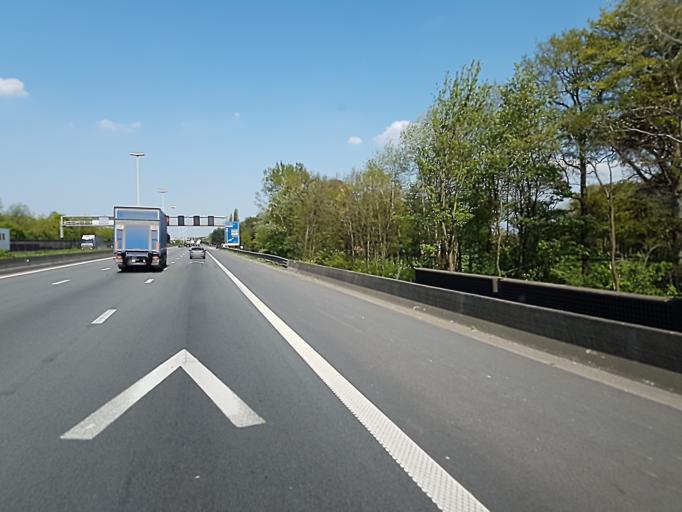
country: BE
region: Flanders
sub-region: Provincie Oost-Vlaanderen
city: Merelbeke
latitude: 50.9986
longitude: 3.7170
